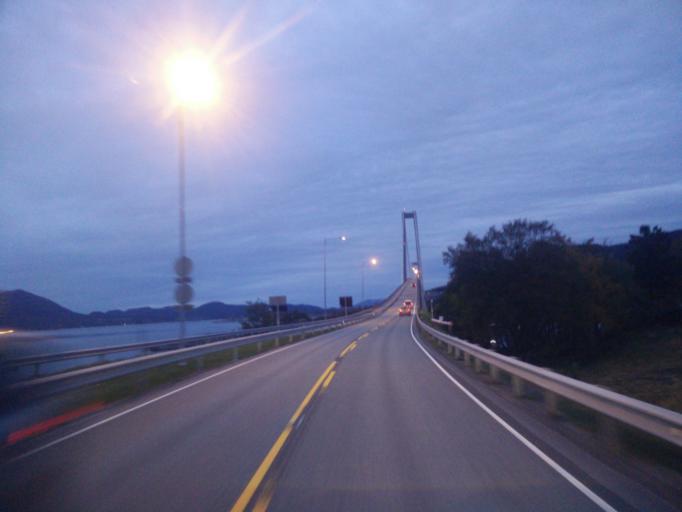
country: NO
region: More og Romsdal
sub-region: Gjemnes
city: Batnfjordsora
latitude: 62.9649
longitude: 7.7695
